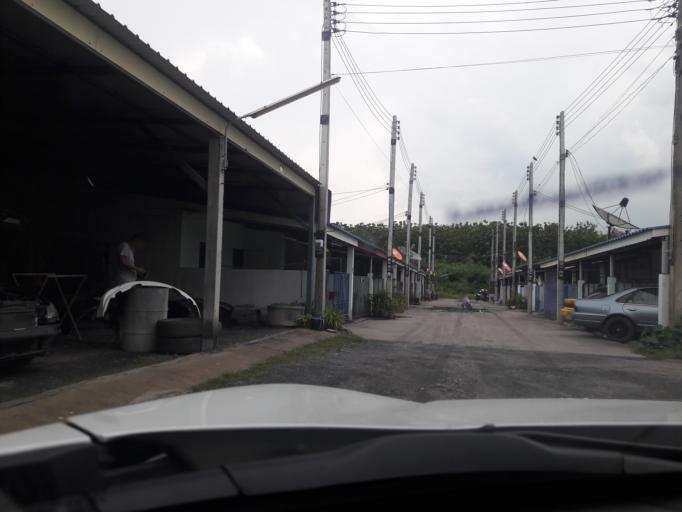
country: TH
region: Lop Buri
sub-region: Amphoe Tha Luang
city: Tha Luang
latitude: 15.0653
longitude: 101.1258
